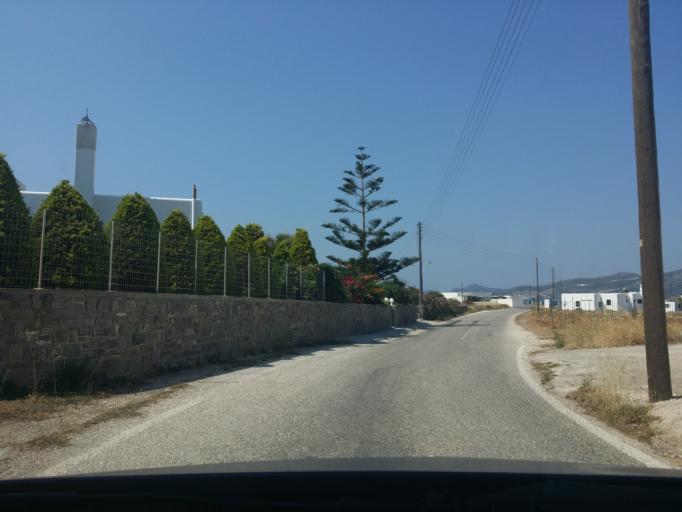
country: GR
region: South Aegean
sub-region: Nomos Kykladon
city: Antiparos
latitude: 37.0256
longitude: 25.1081
